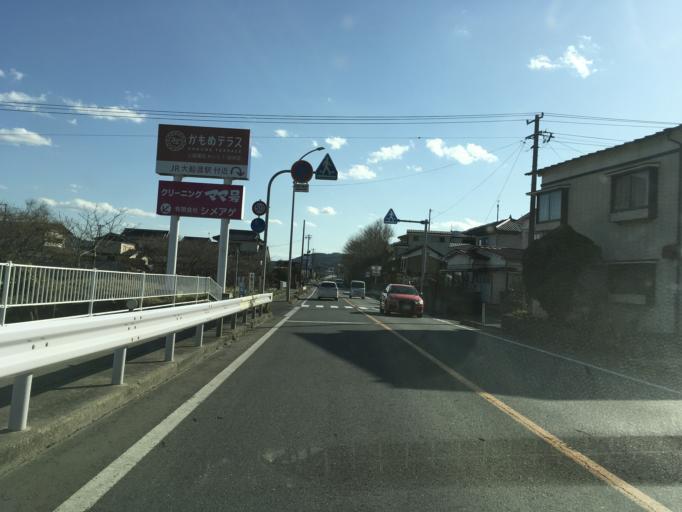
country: JP
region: Iwate
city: Ofunato
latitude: 39.0407
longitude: 141.7211
